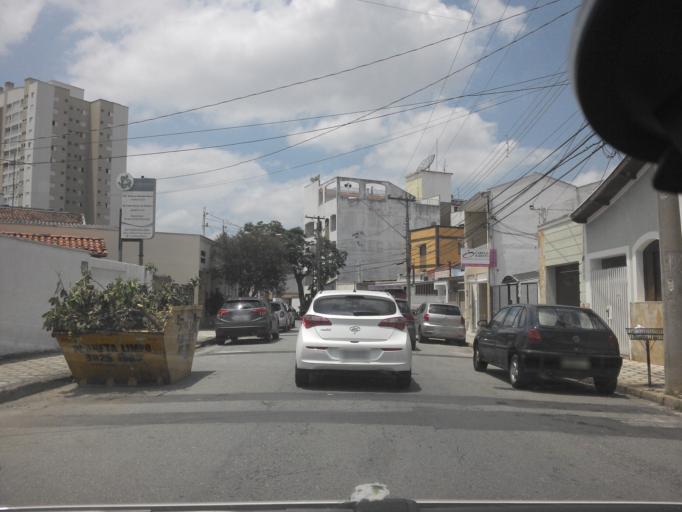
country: BR
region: Sao Paulo
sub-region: Taubate
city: Taubate
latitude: -23.0337
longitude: -45.5629
